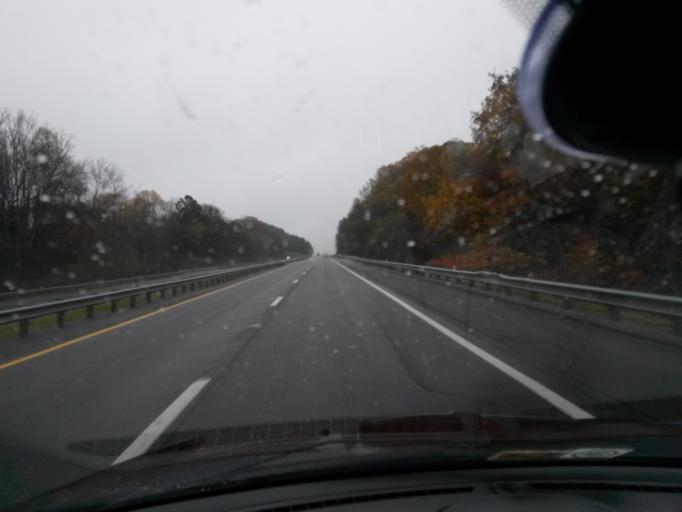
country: US
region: Virginia
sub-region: Montgomery County
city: Christiansburg
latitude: 37.1424
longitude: -80.3869
